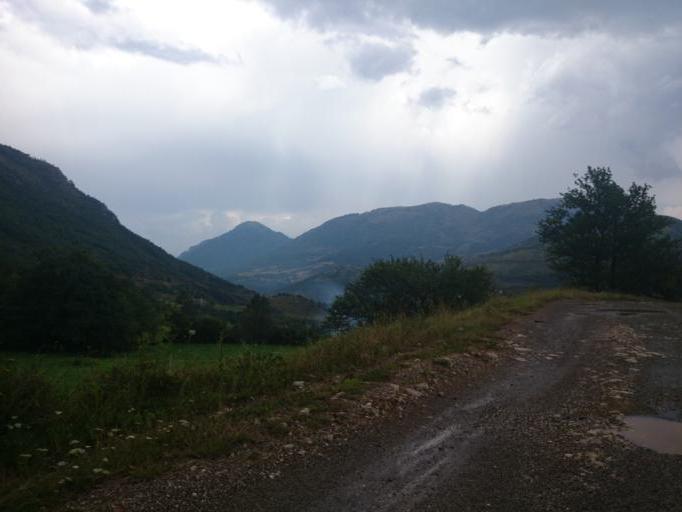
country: AL
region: Diber
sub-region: Rrethi i Dibres
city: Fushe-Lure
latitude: 41.8360
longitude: 20.1773
